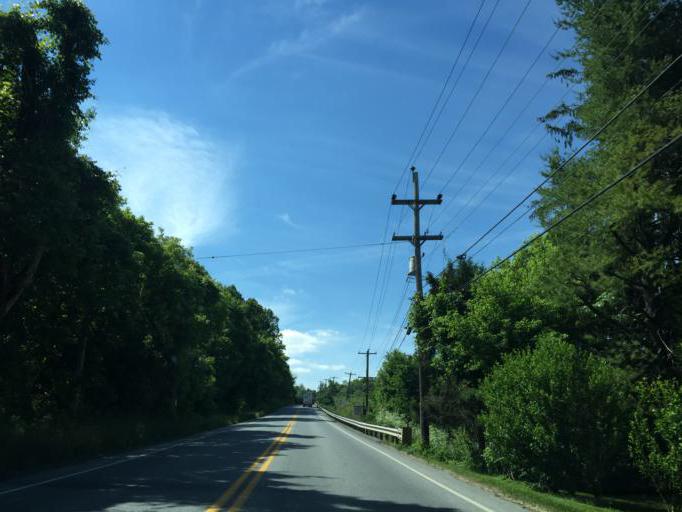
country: US
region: Pennsylvania
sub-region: York County
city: Susquehanna Trails
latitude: 39.7685
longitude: -76.3304
